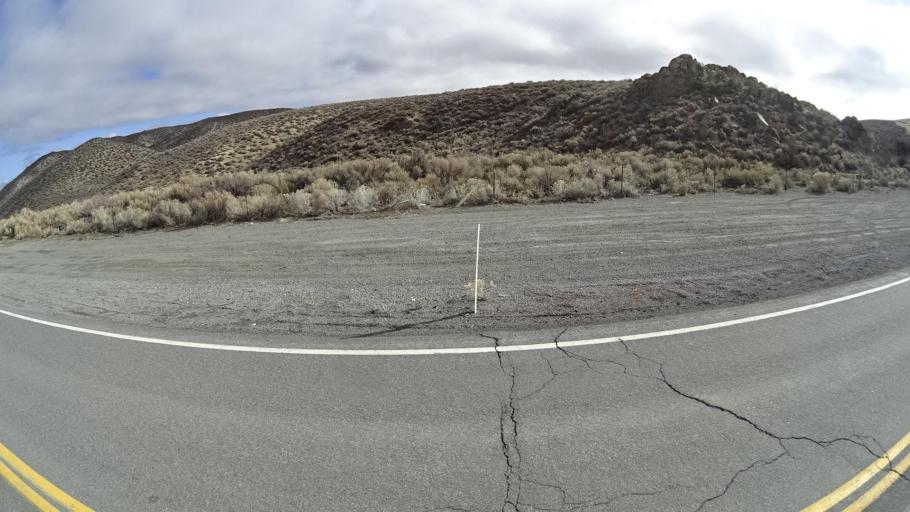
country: US
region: Nevada
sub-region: Washoe County
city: Cold Springs
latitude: 39.8042
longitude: -119.9311
